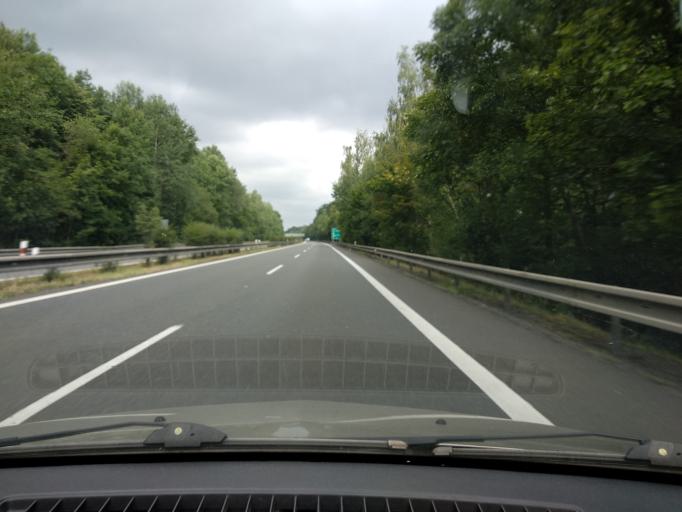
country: CZ
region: Olomoucky
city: Litovel
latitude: 49.7071
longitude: 17.0284
